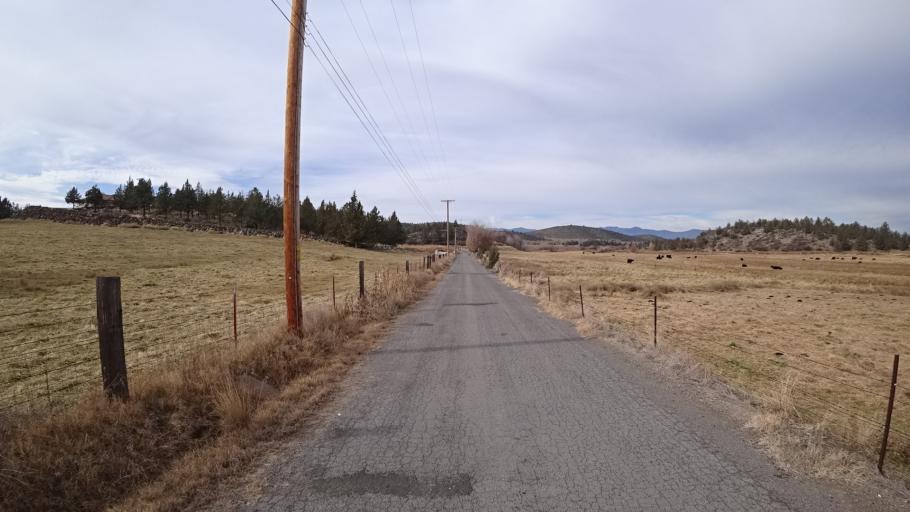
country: US
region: California
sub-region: Siskiyou County
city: Montague
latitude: 41.6833
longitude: -122.5208
